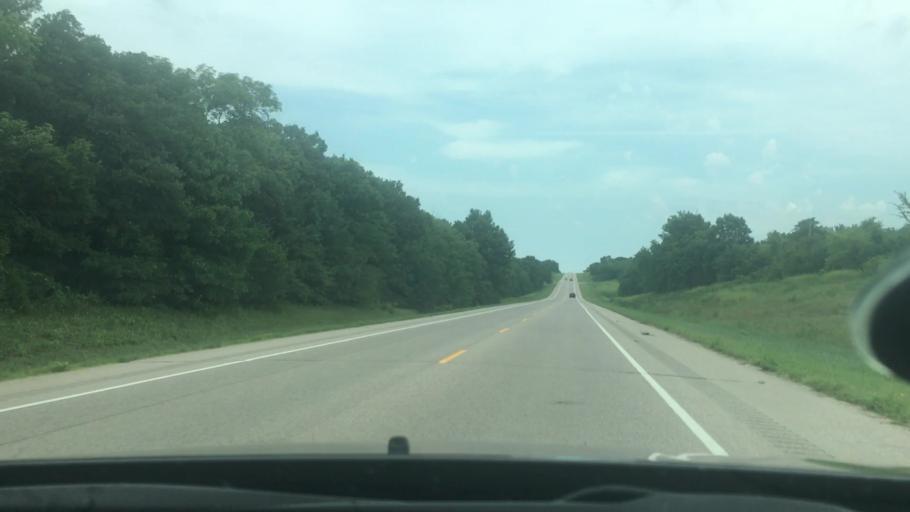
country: US
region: Oklahoma
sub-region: Seminole County
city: Konawa
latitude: 35.0049
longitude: -96.6788
